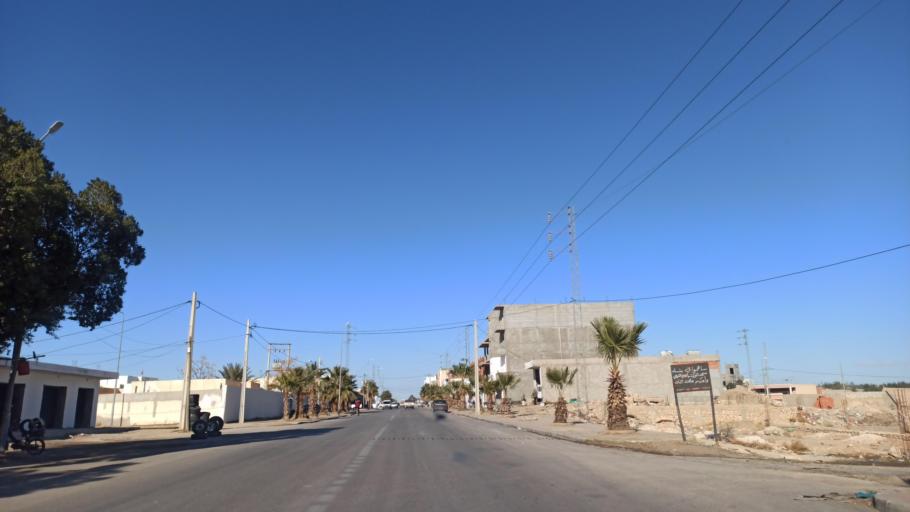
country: TN
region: Sidi Bu Zayd
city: Jilma
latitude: 35.2770
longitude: 9.4190
